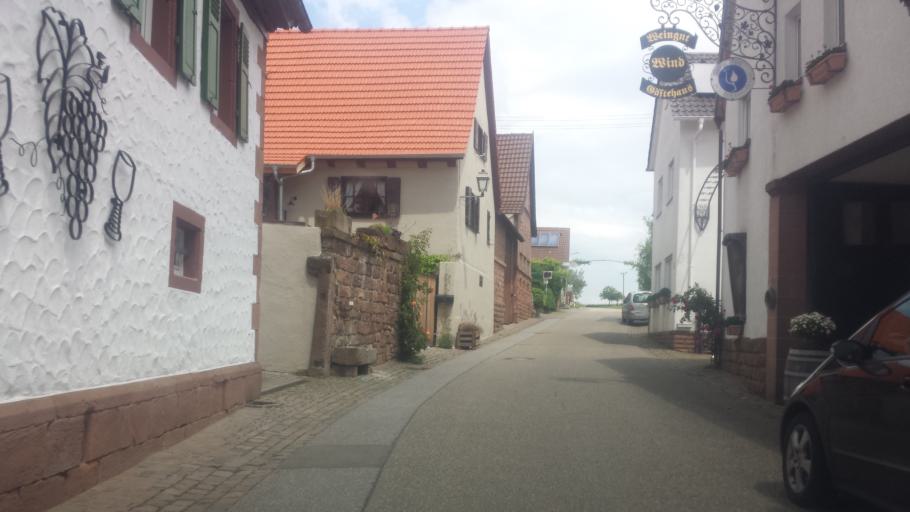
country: DE
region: Rheinland-Pfalz
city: Eschbach
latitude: 49.1756
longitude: 8.0213
